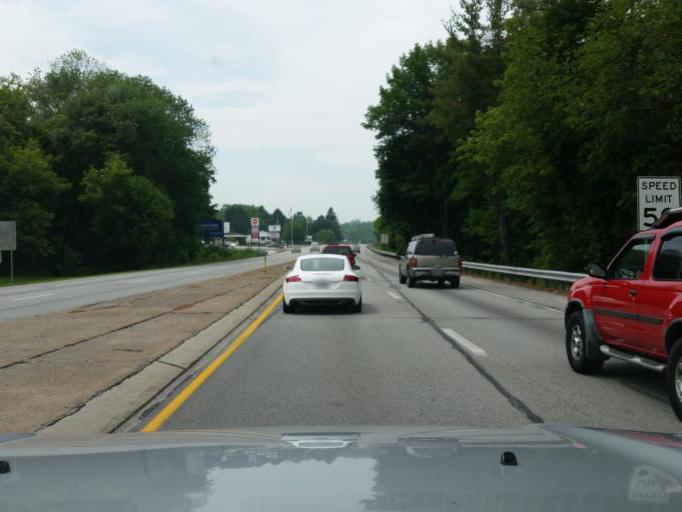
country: US
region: Pennsylvania
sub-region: York County
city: Dillsburg
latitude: 40.1090
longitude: -77.0411
